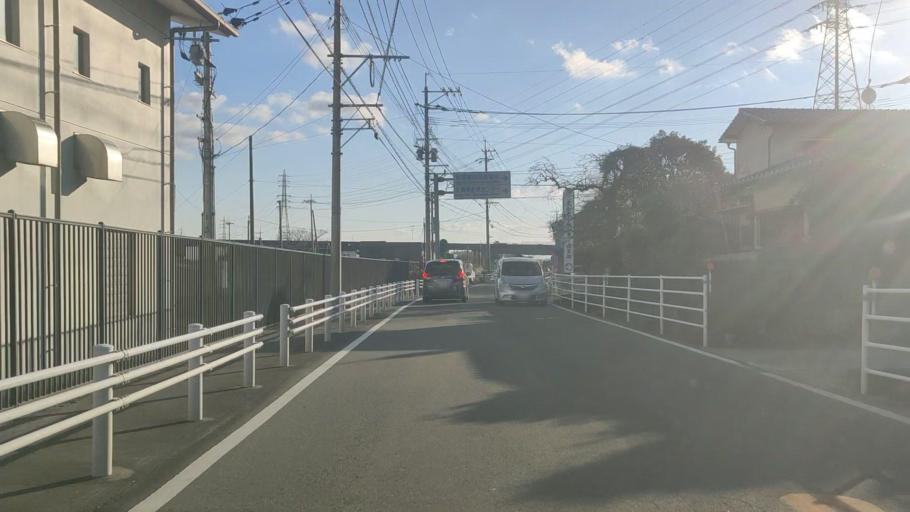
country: JP
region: Saga Prefecture
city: Saga-shi
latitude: 33.3208
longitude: 130.2675
